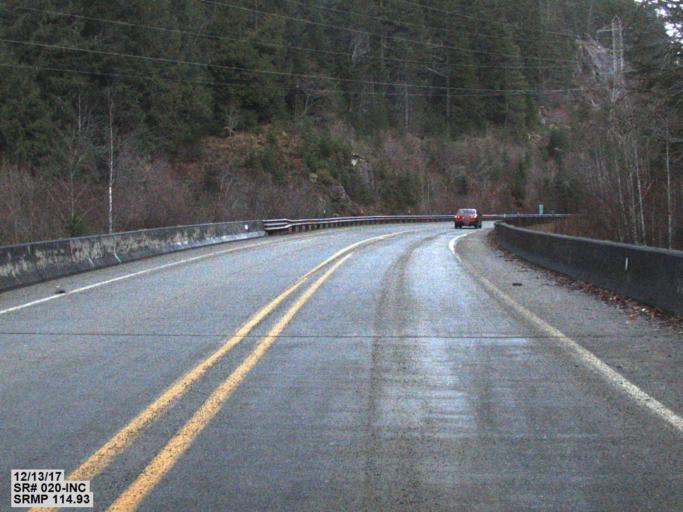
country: US
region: Washington
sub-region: Snohomish County
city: Darrington
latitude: 48.6272
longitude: -121.3382
